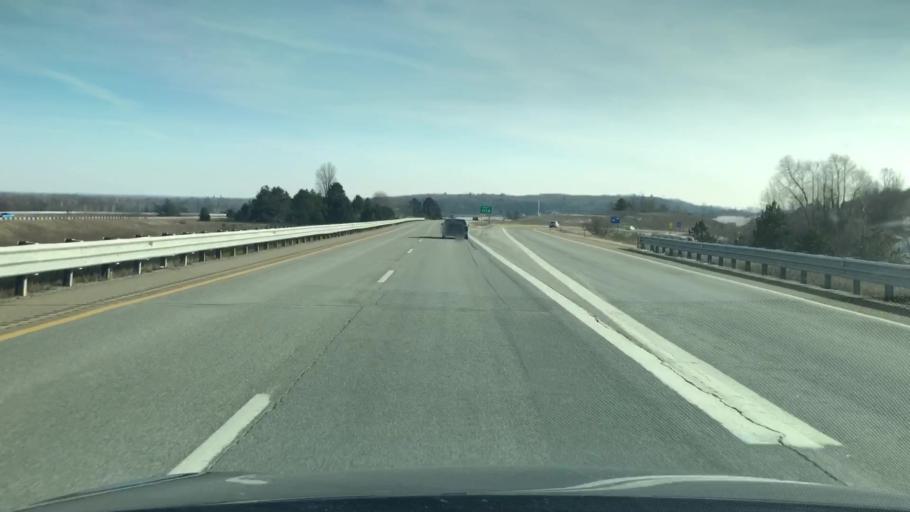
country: US
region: Michigan
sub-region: Ogemaw County
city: West Branch
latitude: 44.2457
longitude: -84.2304
